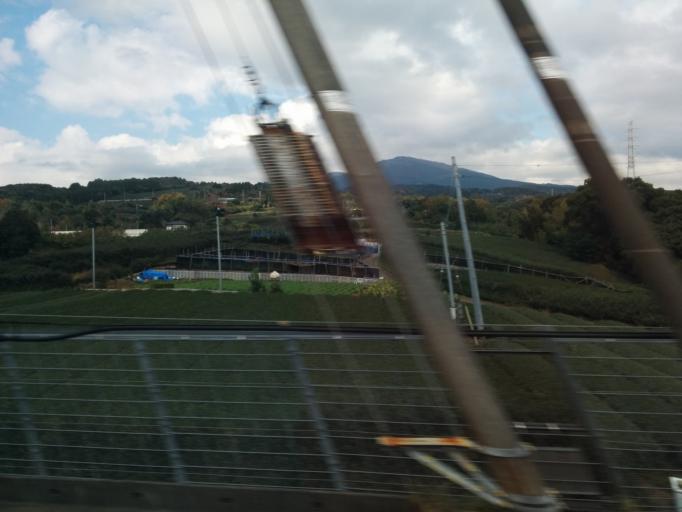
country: JP
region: Shizuoka
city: Numazu
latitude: 35.1473
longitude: 138.7914
